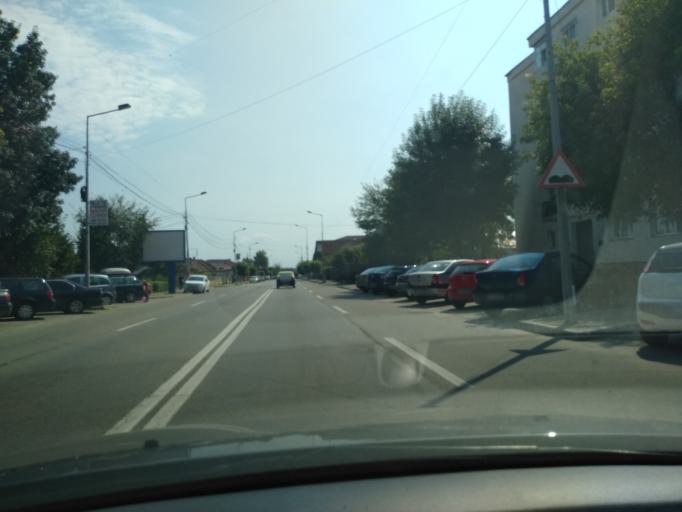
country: RO
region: Gorj
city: Targu Jiu
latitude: 45.0236
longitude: 23.2685
